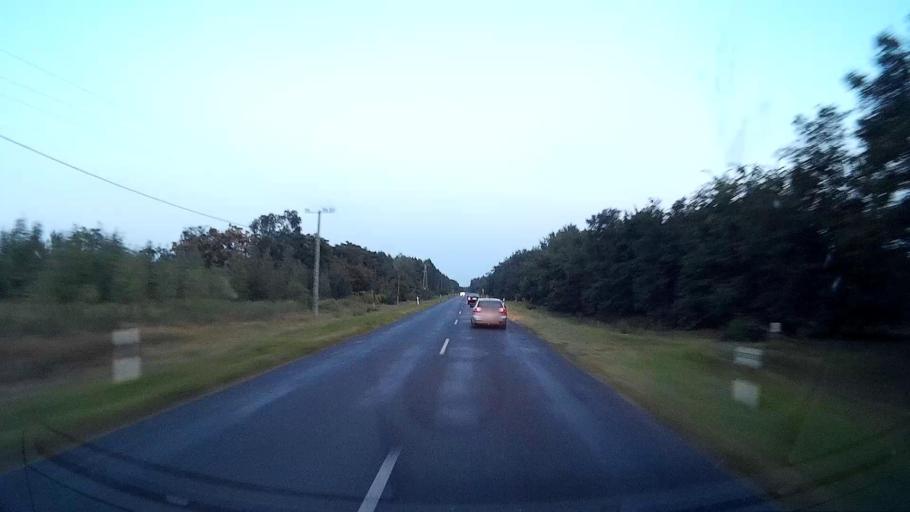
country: HU
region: Pest
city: Cegledbercel
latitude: 47.2037
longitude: 19.6964
